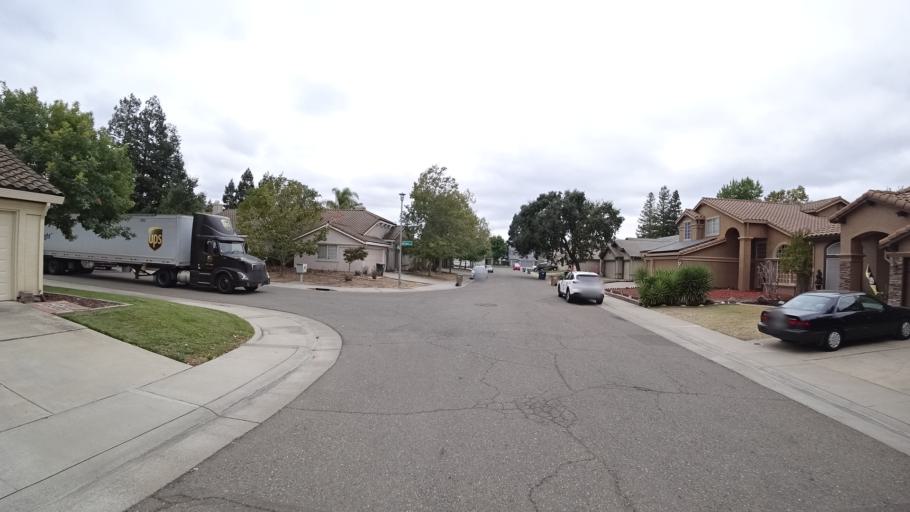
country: US
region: California
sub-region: Sacramento County
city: Laguna
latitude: 38.4194
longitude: -121.4518
